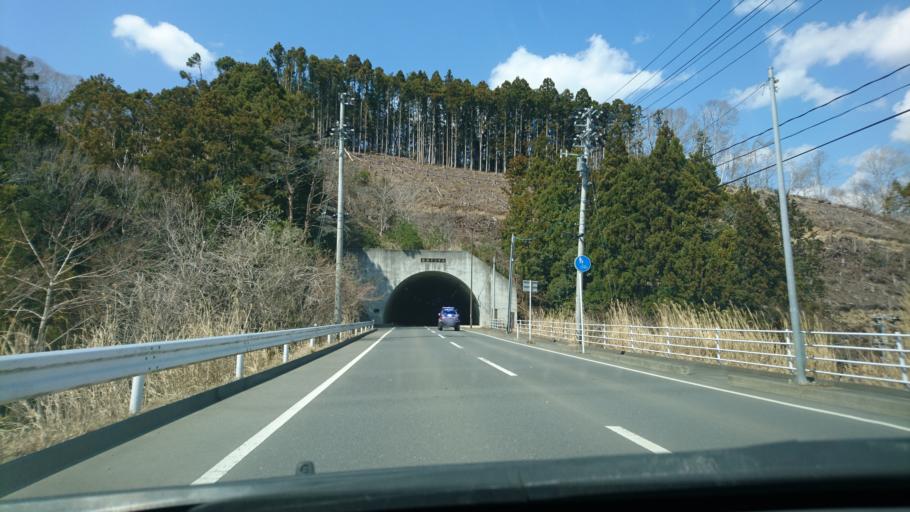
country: JP
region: Miyagi
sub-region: Oshika Gun
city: Onagawa Cho
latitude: 38.4974
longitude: 141.4862
